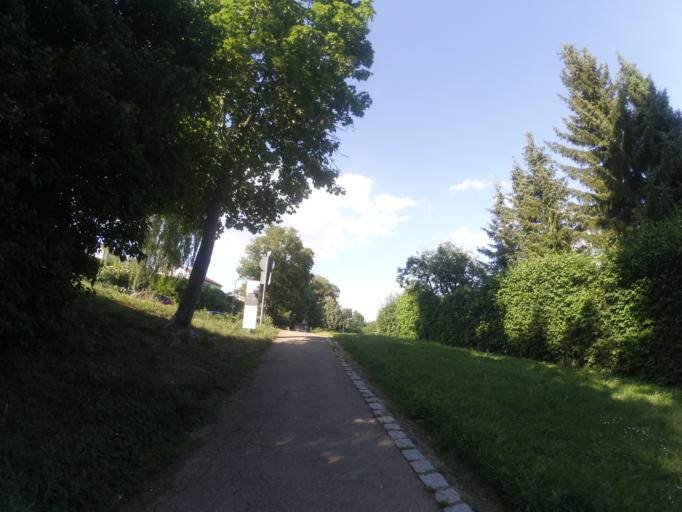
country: DE
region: Baden-Wuerttemberg
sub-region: Tuebingen Region
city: Ulm
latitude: 48.4201
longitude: 10.0076
